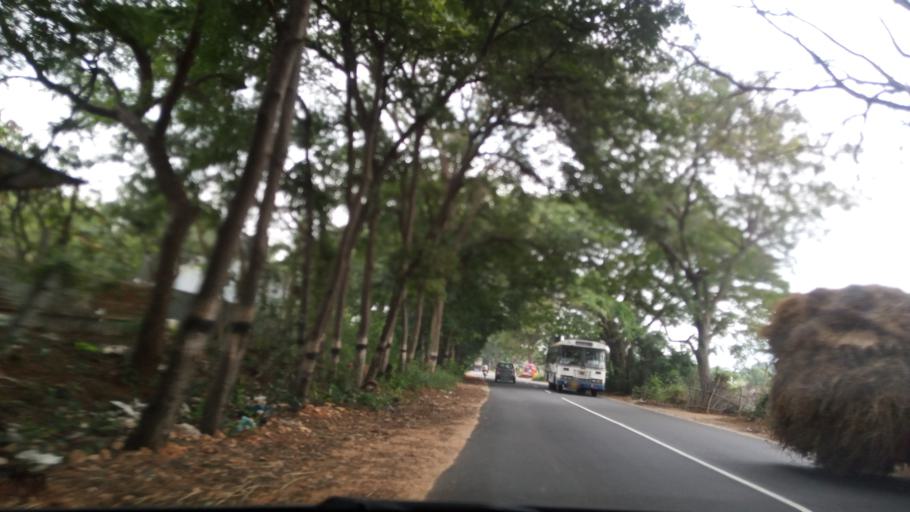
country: IN
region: Andhra Pradesh
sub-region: Chittoor
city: Madanapalle
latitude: 13.6366
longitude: 78.5838
